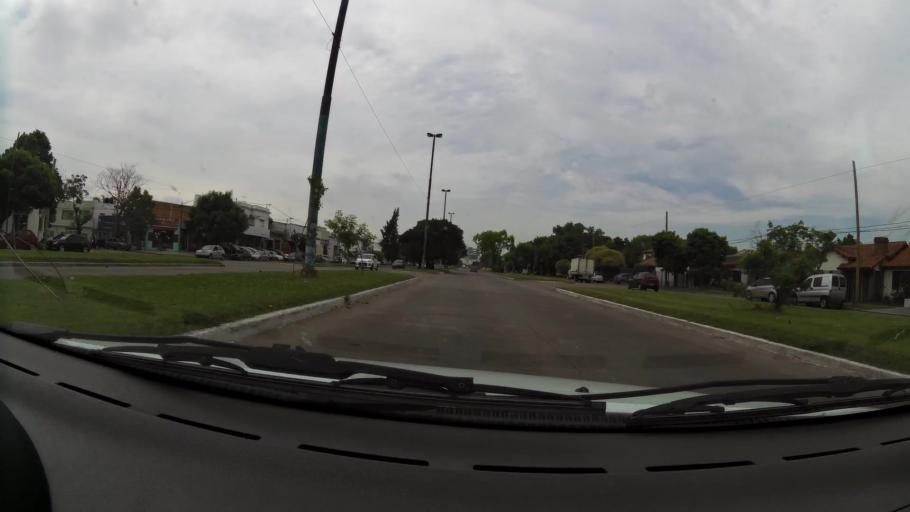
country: AR
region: Buenos Aires
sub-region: Partido de La Plata
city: La Plata
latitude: -34.9029
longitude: -57.9799
